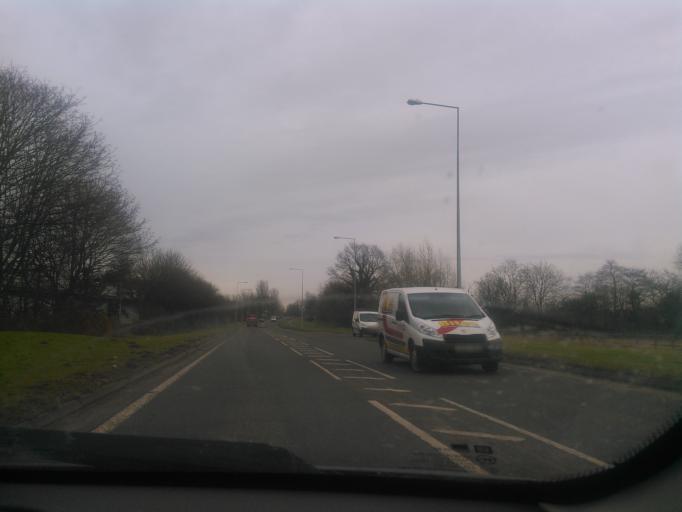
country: GB
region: England
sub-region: Telford and Wrekin
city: Oakengates
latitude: 52.7140
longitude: -2.4622
